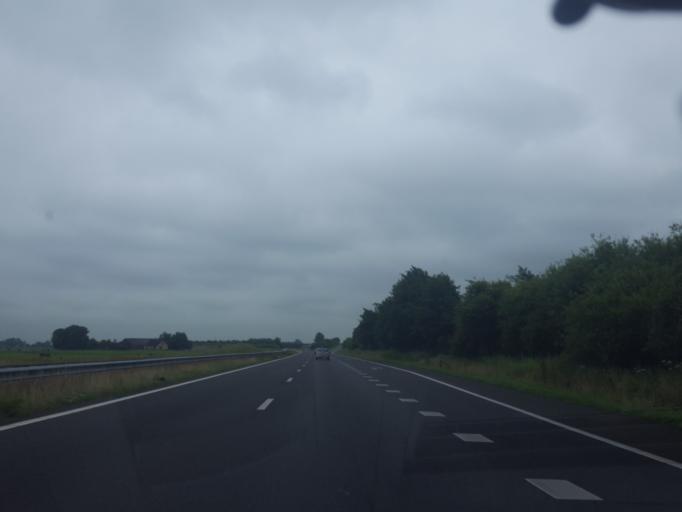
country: NL
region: Friesland
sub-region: Gemeente Boarnsterhim
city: Reduzum
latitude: 53.1191
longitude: 5.8089
